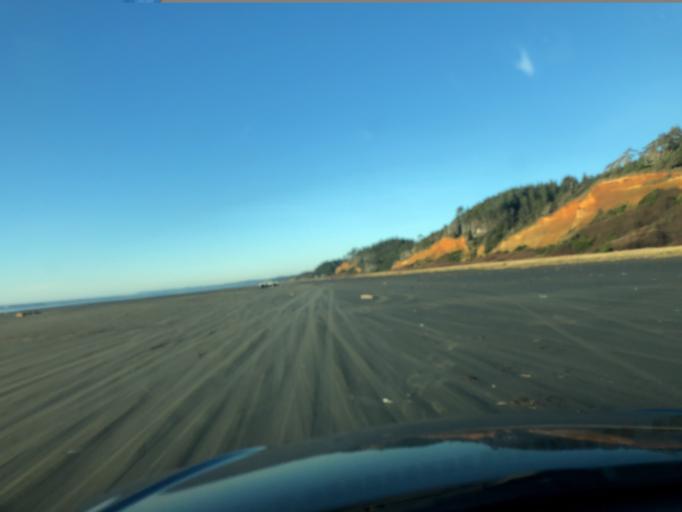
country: US
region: Washington
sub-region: Grays Harbor County
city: Ocean Shores
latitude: 47.1683
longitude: -124.1955
